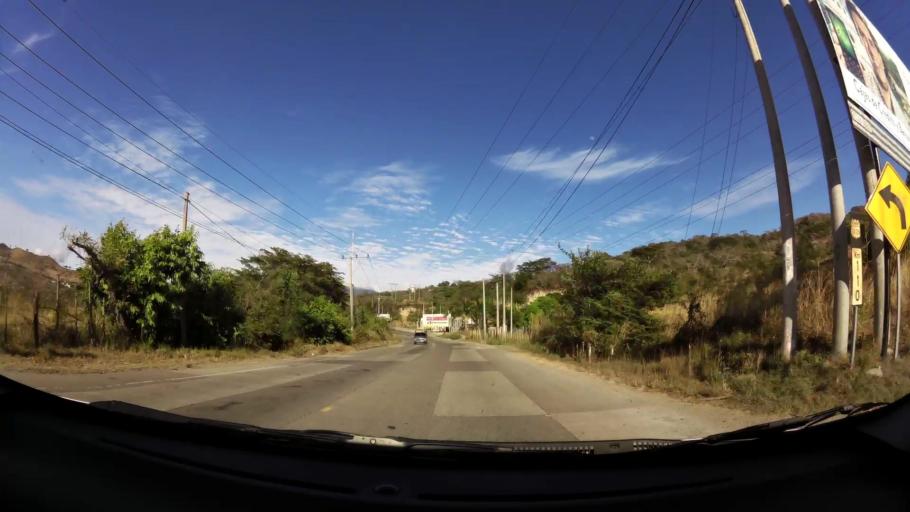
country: SV
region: Santa Ana
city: Metapan
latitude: 14.3045
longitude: -89.4556
